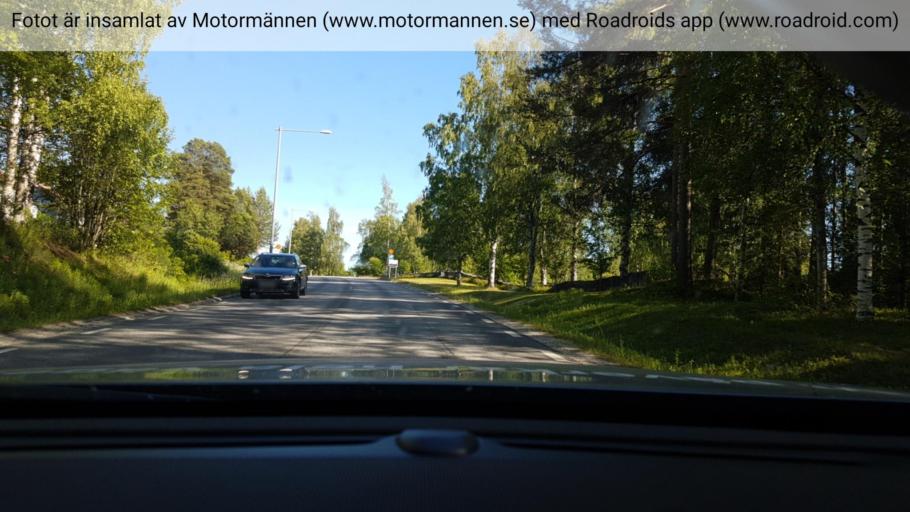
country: SE
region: Vaesterbotten
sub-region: Lycksele Kommun
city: Lycksele
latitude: 64.6087
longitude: 18.6481
